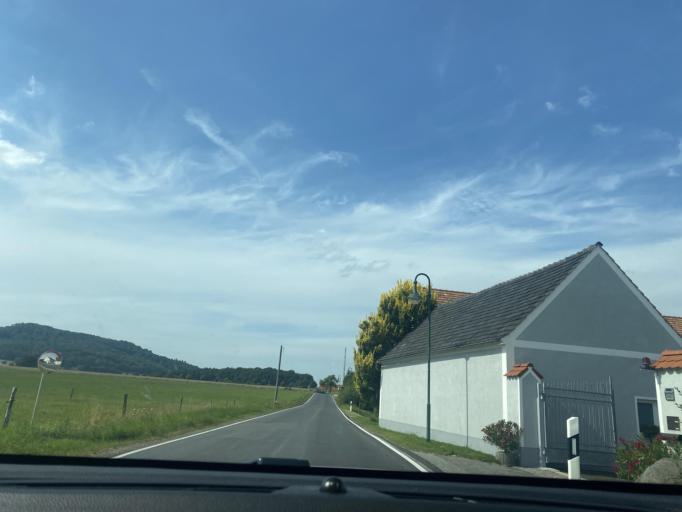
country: DE
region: Saxony
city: Sohland am Rotstein
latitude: 51.0964
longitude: 14.7913
